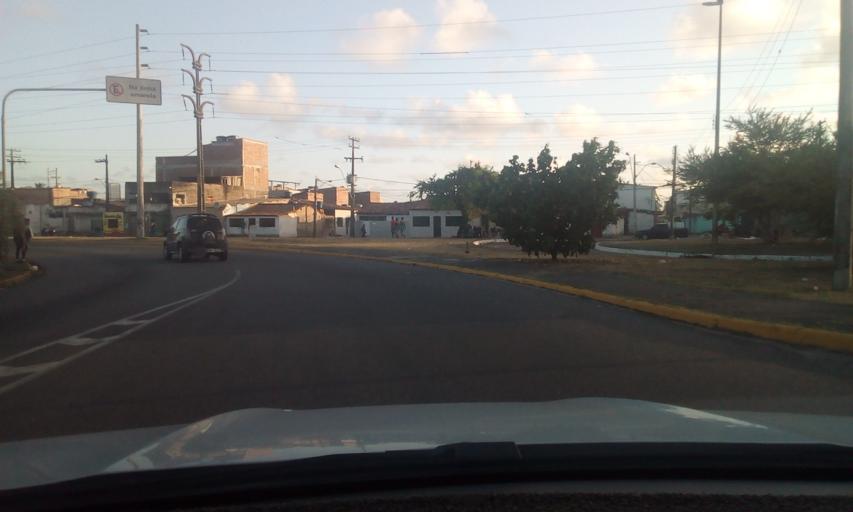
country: BR
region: Pernambuco
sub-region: Recife
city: Recife
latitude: -8.0691
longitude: -34.8981
